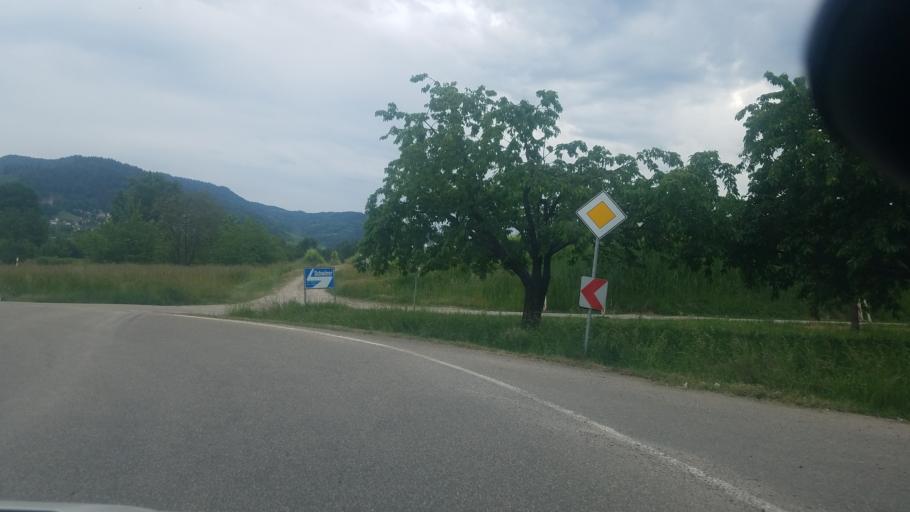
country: DE
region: Baden-Wuerttemberg
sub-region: Freiburg Region
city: Kappelrodeck
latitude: 48.6039
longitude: 8.1075
